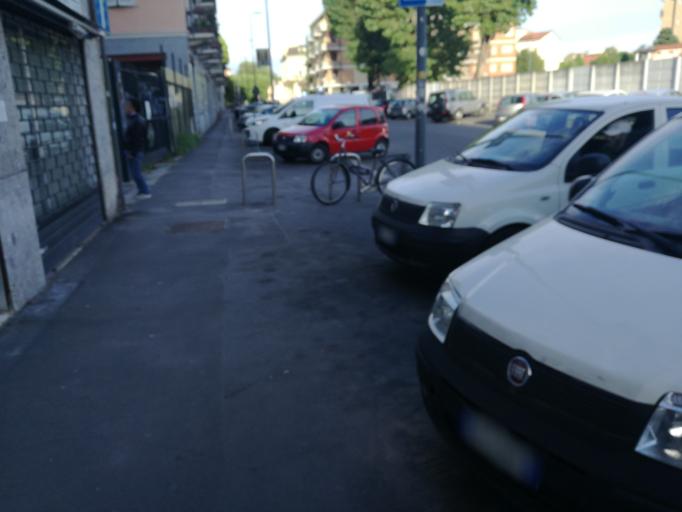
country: IT
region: Lombardy
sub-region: Citta metropolitana di Milano
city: Milano
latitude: 45.4331
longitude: 9.1794
